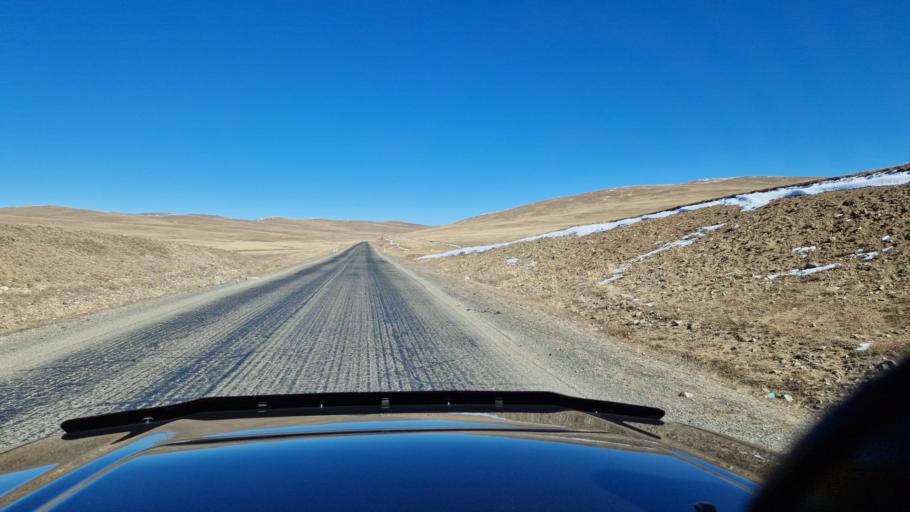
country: MN
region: Hentiy
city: Modot
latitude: 47.7798
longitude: 108.6619
